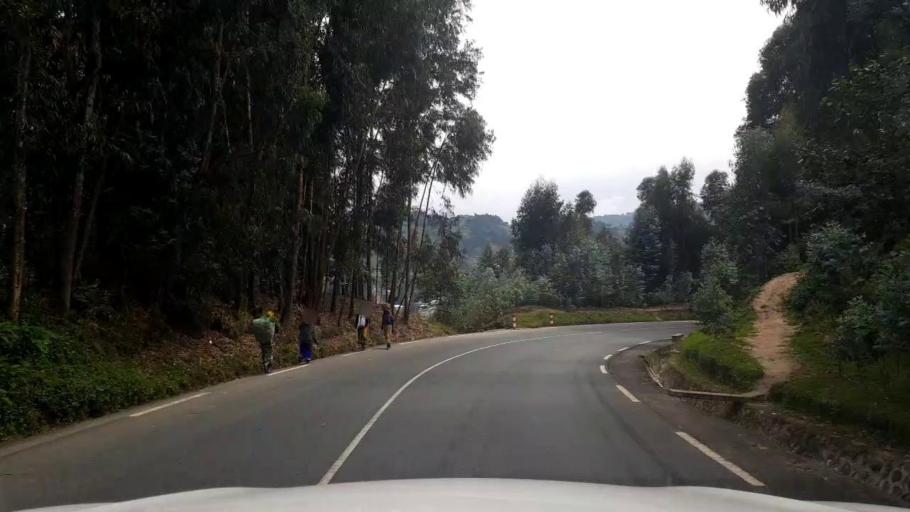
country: RW
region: Northern Province
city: Musanze
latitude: -1.6777
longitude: 29.5177
